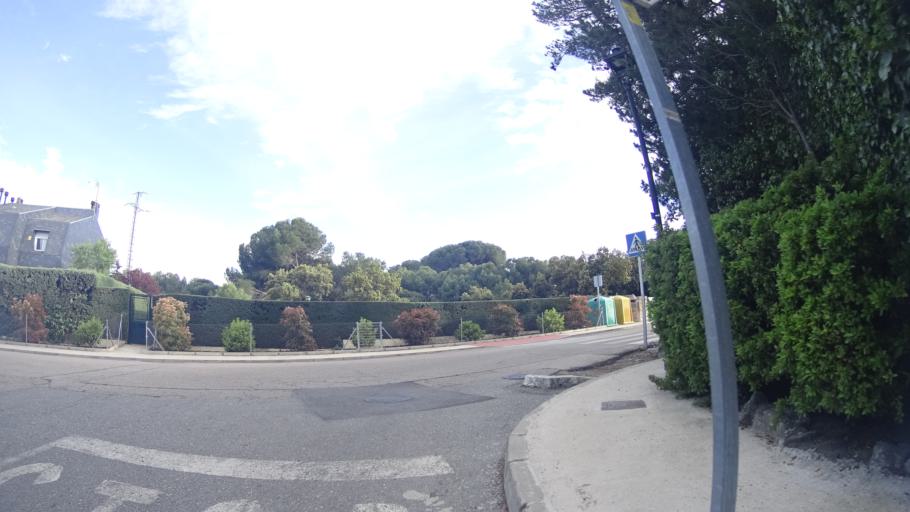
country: ES
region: Madrid
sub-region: Provincia de Madrid
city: Galapagar
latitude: 40.5837
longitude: -3.9694
